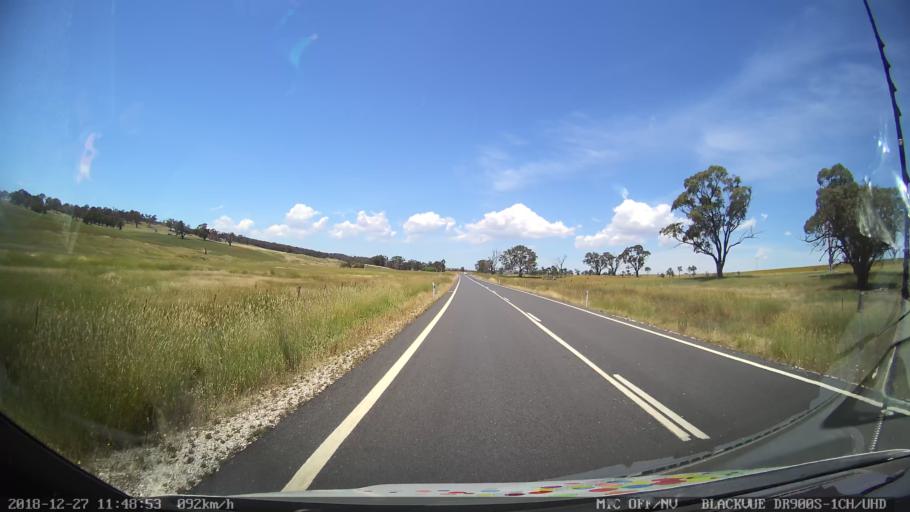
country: AU
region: New South Wales
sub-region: Bathurst Regional
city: Perthville
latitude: -33.6125
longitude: 149.4350
